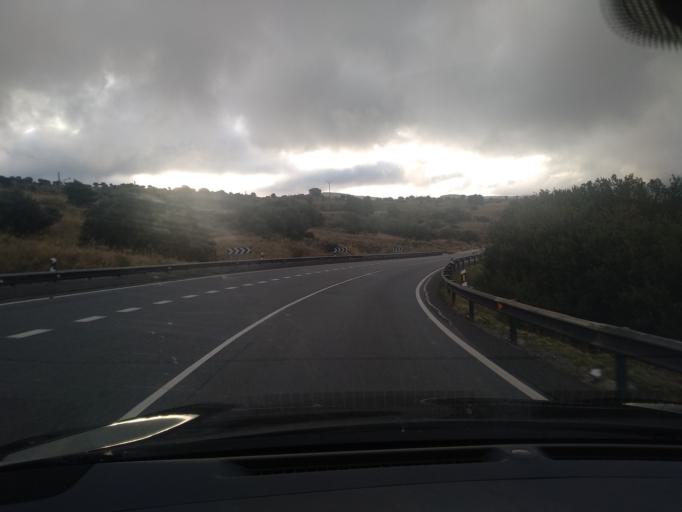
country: ES
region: Castille and Leon
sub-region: Provincia de Segovia
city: Otero de Herreros
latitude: 40.7730
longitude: -4.2028
